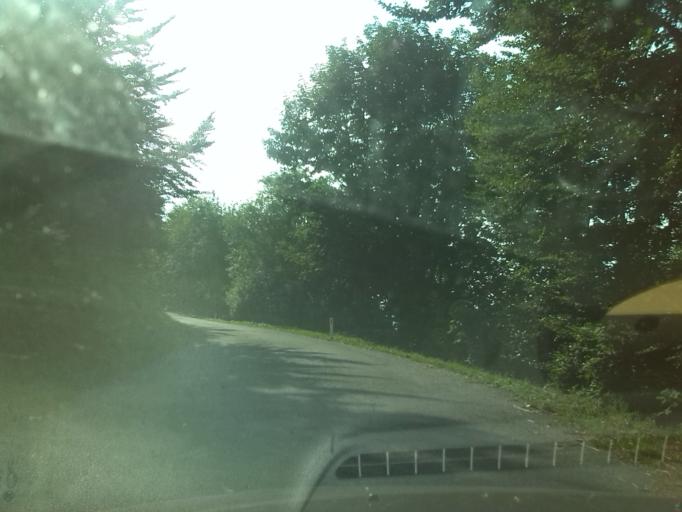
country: IT
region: Friuli Venezia Giulia
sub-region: Provincia di Udine
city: Cras
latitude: 46.1923
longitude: 13.6349
